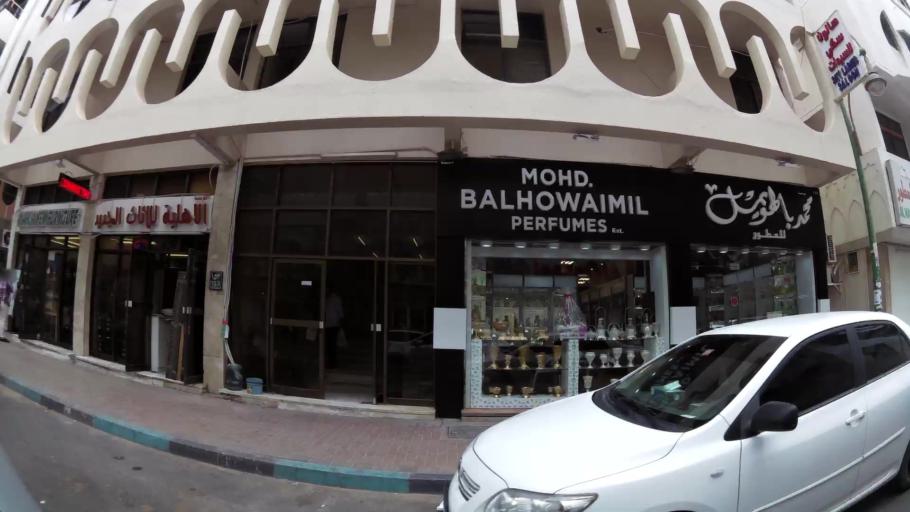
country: AE
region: Abu Dhabi
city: Al Ain
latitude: 24.2247
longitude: 55.7626
